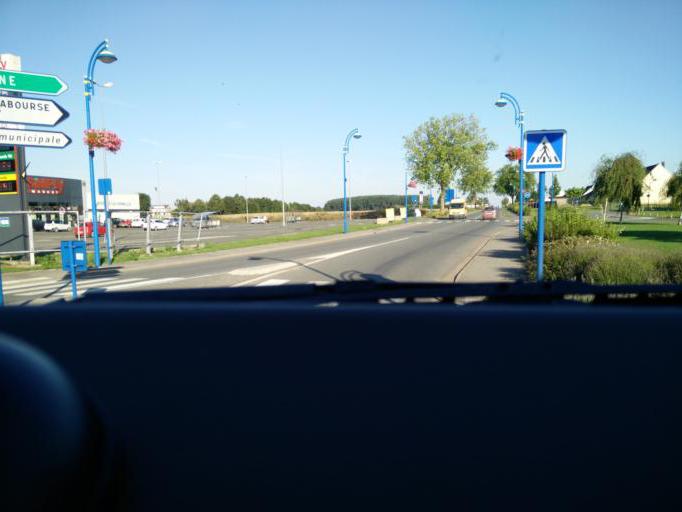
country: FR
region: Nord-Pas-de-Calais
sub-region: Departement du Pas-de-Calais
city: Noyelles-les-Vermelles
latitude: 50.4826
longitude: 2.7283
